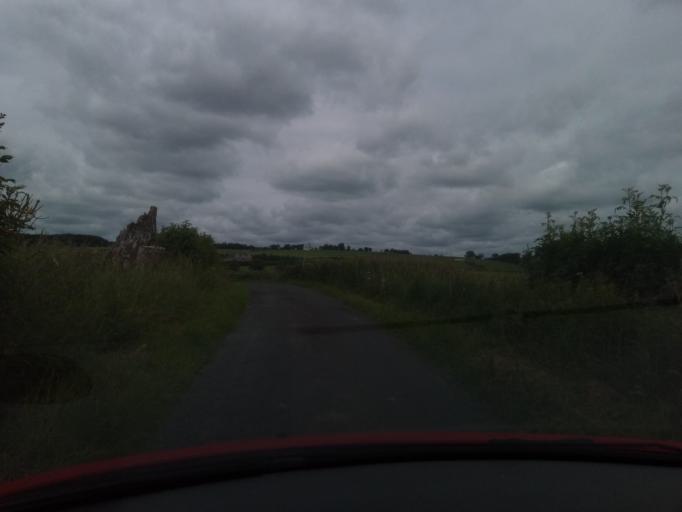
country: GB
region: Scotland
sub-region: The Scottish Borders
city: Hawick
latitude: 55.4557
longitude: -2.7460
